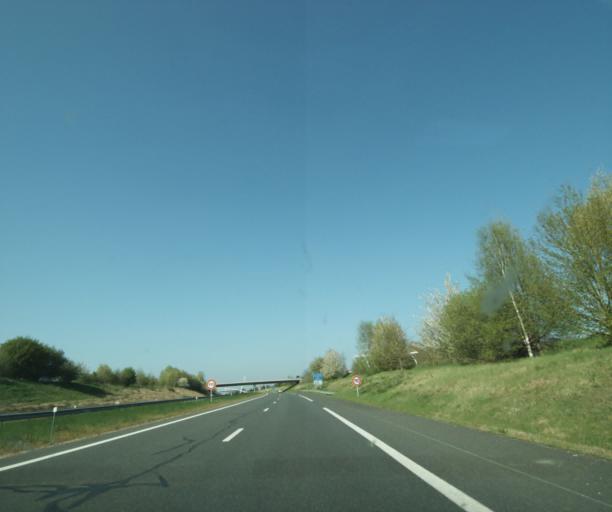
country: FR
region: Centre
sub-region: Departement du Loiret
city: Dordives
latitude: 48.1703
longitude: 2.7662
